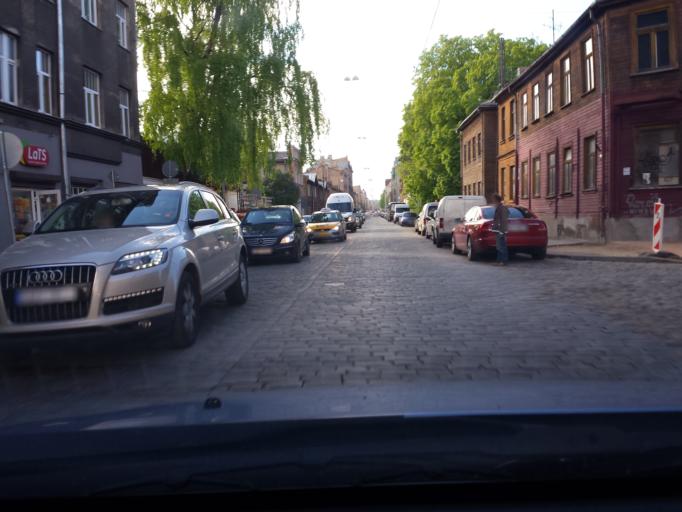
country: LV
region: Riga
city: Riga
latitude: 56.9511
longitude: 24.1462
